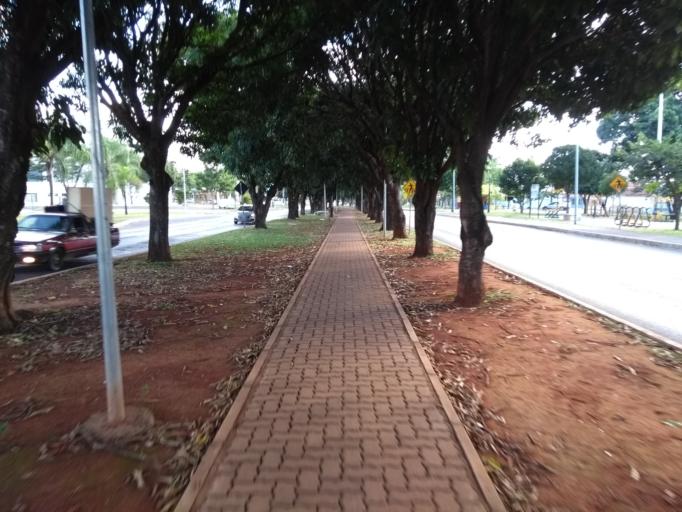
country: BR
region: Federal District
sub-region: Brasilia
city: Brasilia
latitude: -15.7913
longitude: -47.9385
